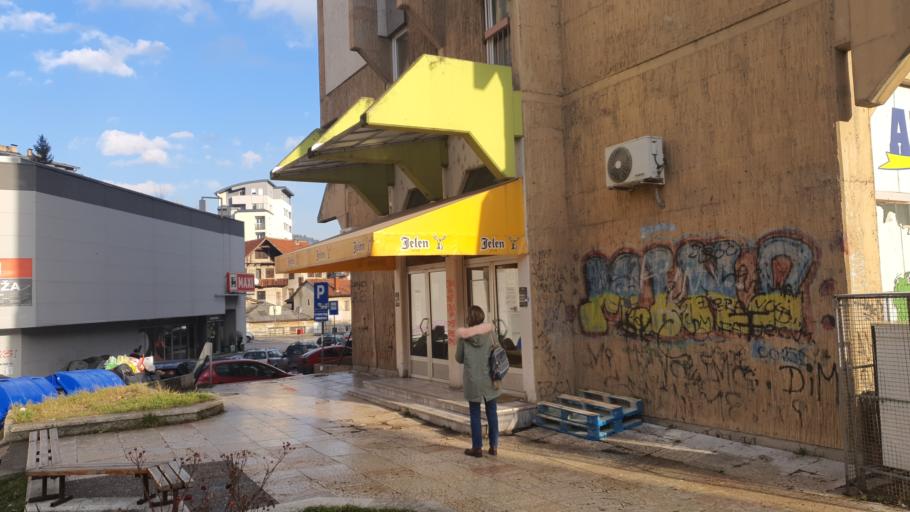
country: RS
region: Central Serbia
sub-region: Zlatiborski Okrug
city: Uzice
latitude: 43.8561
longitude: 19.8345
